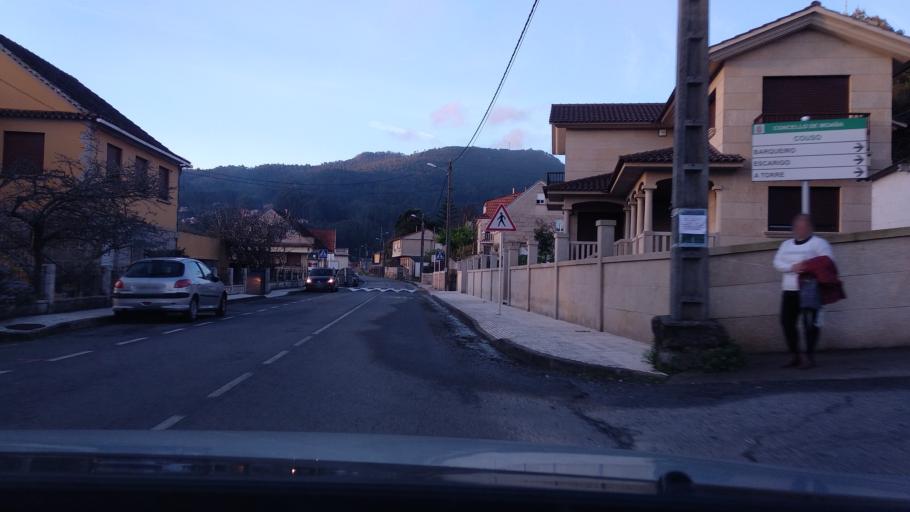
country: ES
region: Galicia
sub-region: Provincia de Pontevedra
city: Moana
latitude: 42.2972
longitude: -8.7237
